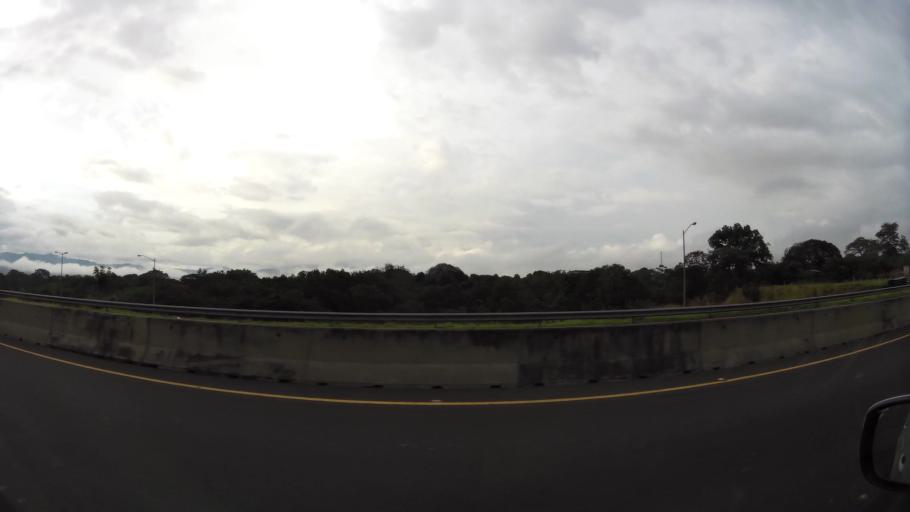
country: CR
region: Alajuela
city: Atenas
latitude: 9.9648
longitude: -84.3142
